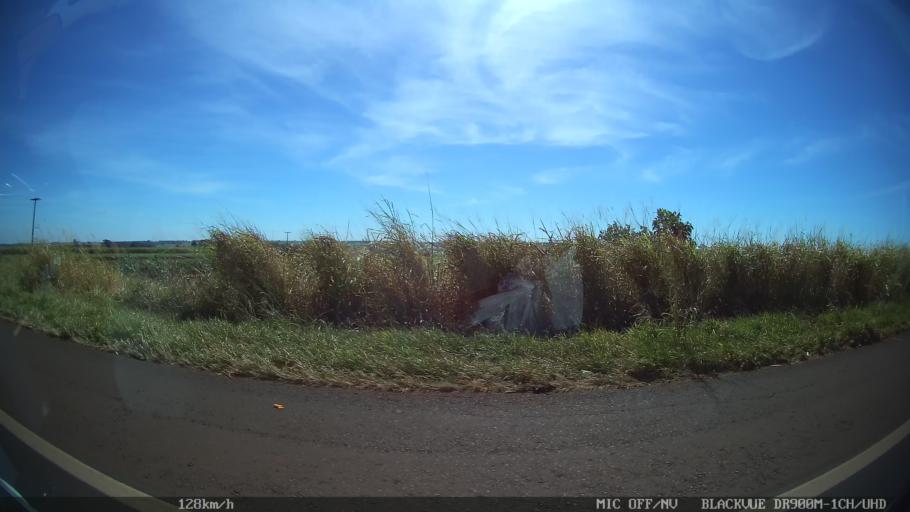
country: BR
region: Sao Paulo
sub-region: Franca
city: Franca
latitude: -20.5601
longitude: -47.6081
